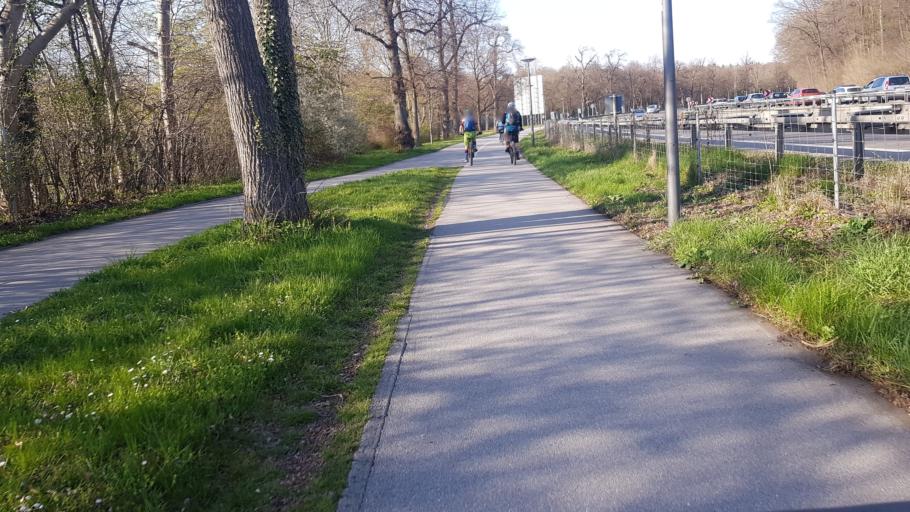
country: DE
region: Bavaria
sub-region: Upper Bavaria
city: Neuried
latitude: 48.0942
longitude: 11.4876
